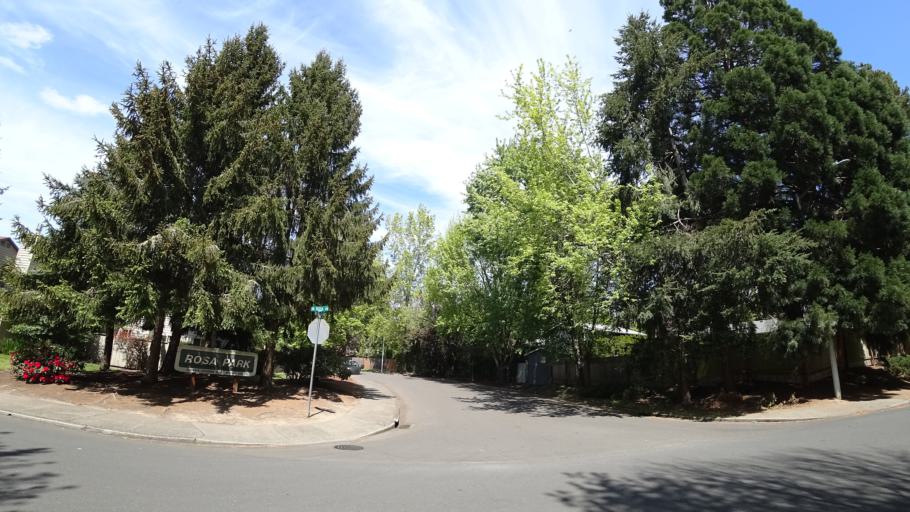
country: US
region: Oregon
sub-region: Washington County
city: Aloha
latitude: 45.4783
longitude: -122.8876
